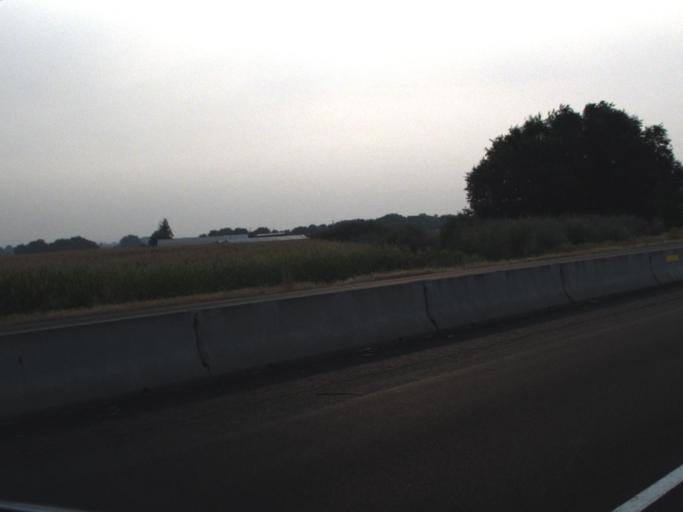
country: US
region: Washington
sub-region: Yakima County
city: Wapato
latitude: 46.4221
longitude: -120.4032
